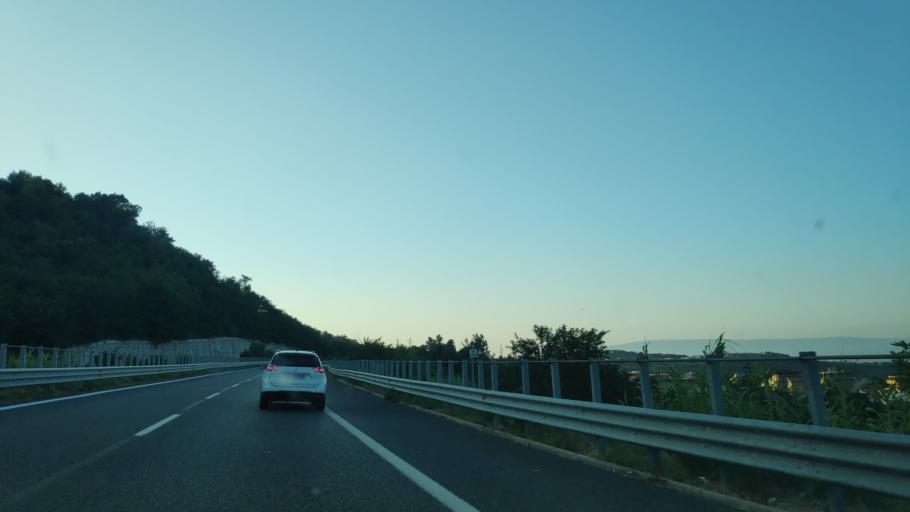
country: IT
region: Calabria
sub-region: Provincia di Reggio Calabria
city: Seminara
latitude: 38.3564
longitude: 15.8661
